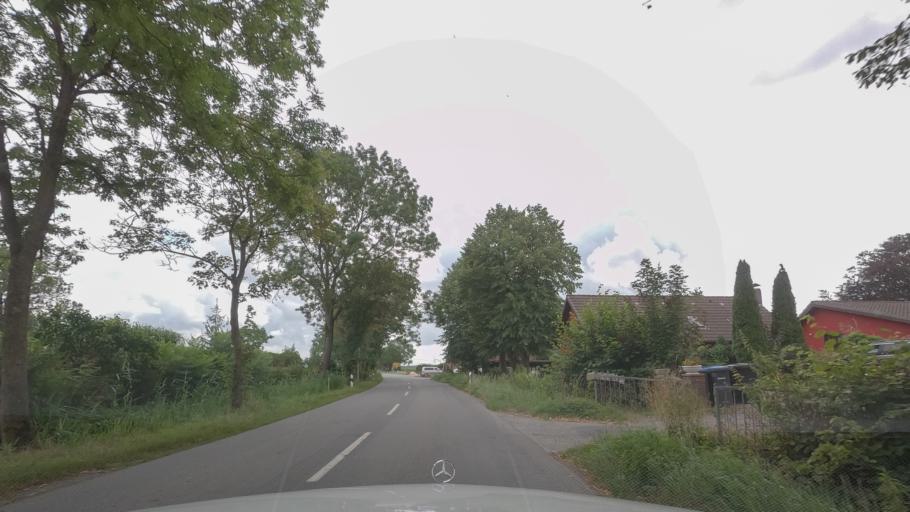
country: DE
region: Lower Saxony
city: Uthlede
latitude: 53.3086
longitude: 8.5350
